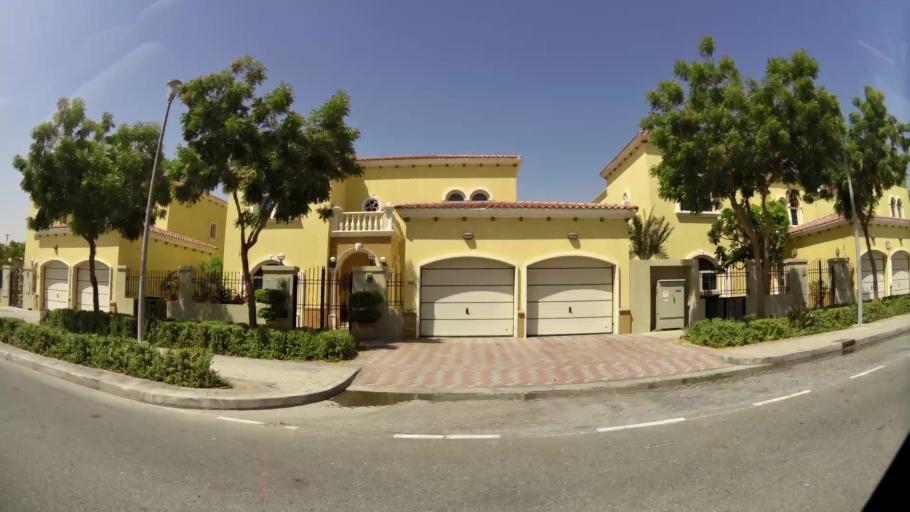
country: AE
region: Dubai
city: Dubai
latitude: 25.0491
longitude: 55.1535
